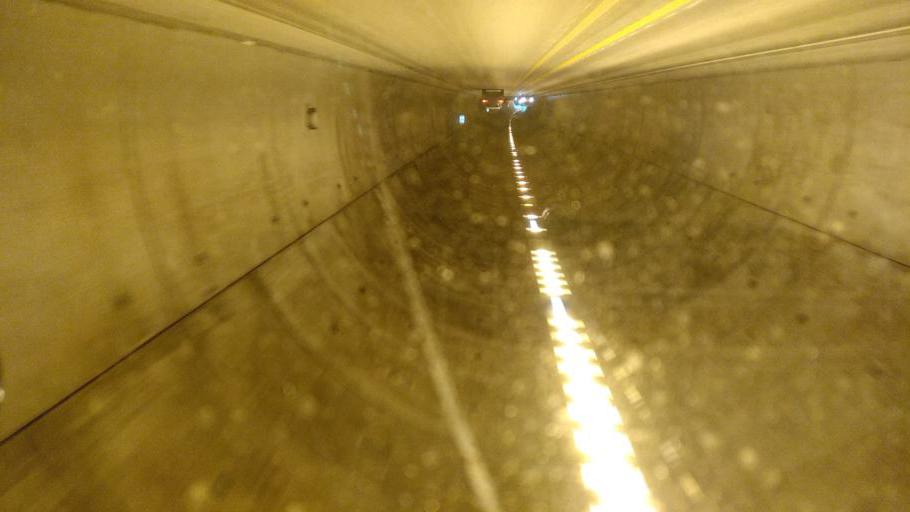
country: NO
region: Rogaland
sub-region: Klepp
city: Kleppe
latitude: 58.7775
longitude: 5.6222
